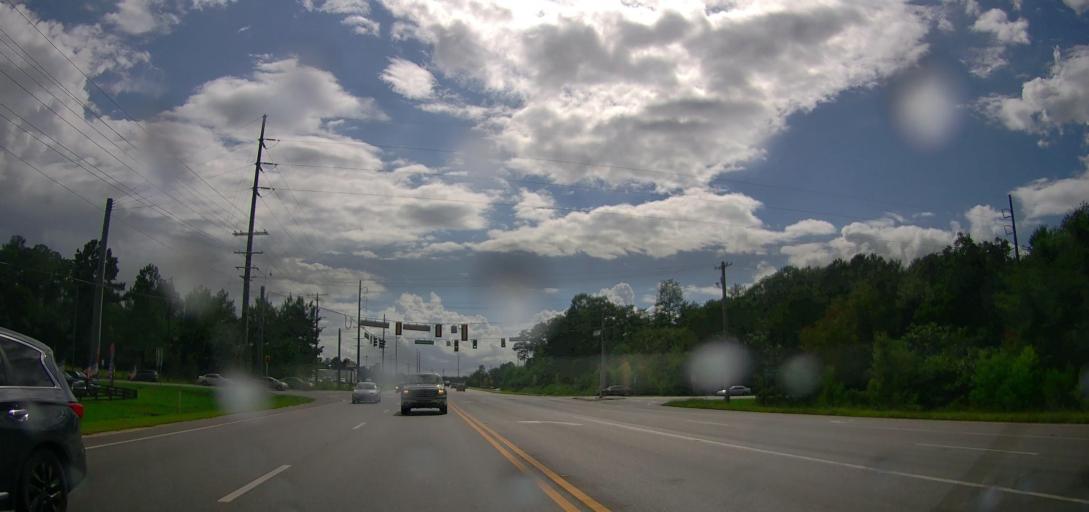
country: US
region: Georgia
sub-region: Coffee County
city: Douglas
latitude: 31.4903
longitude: -82.8356
